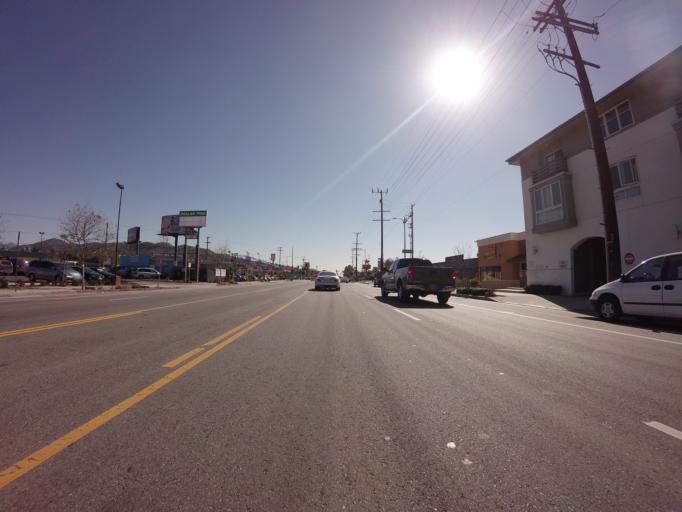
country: US
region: California
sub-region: Los Angeles County
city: North Hollywood
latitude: 34.2310
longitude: -118.3676
